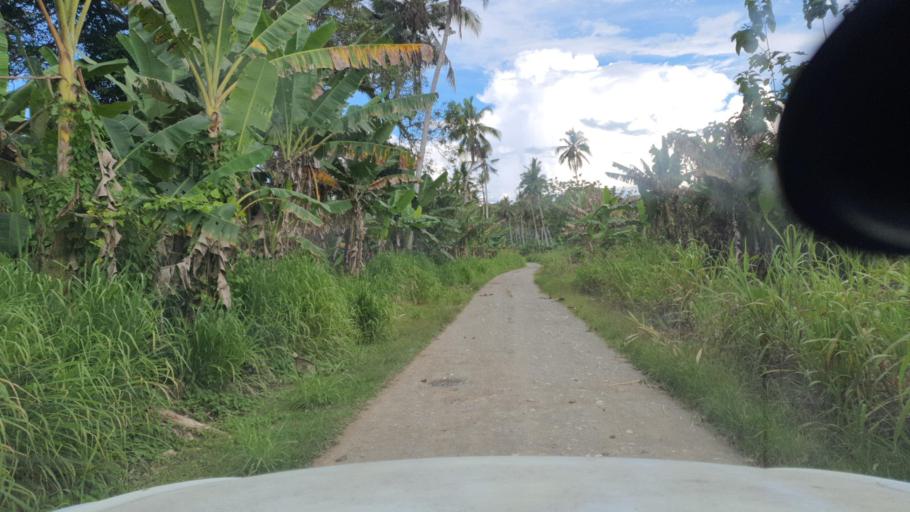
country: SB
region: Guadalcanal
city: Honiara
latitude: -9.3650
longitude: 159.8336
